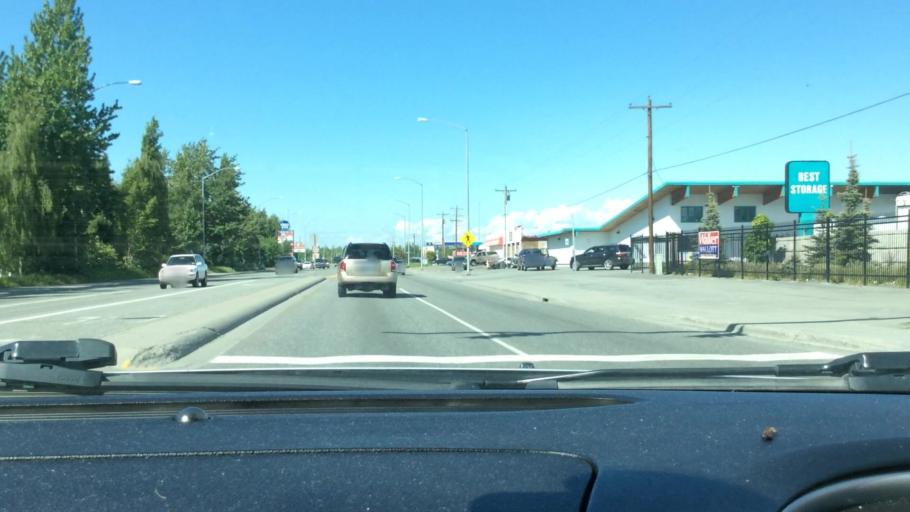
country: US
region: Alaska
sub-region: Anchorage Municipality
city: Anchorage
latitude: 61.2187
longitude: -149.7784
